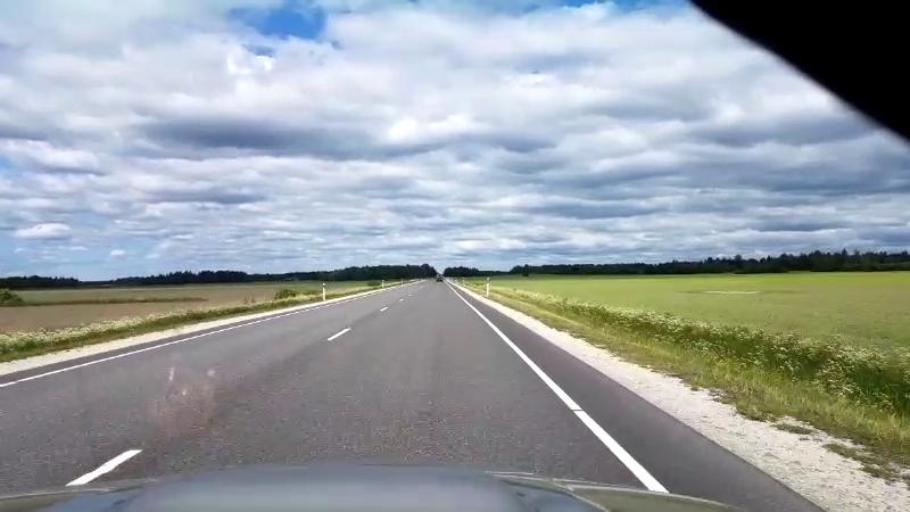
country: EE
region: Raplamaa
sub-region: Maerjamaa vald
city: Marjamaa
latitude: 58.8438
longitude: 24.4261
